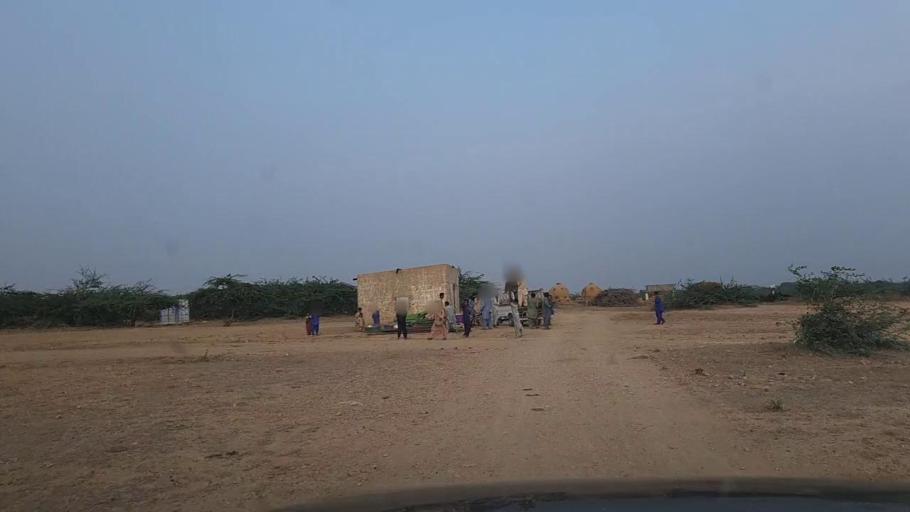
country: PK
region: Sindh
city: Gharo
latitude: 24.7715
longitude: 67.6921
